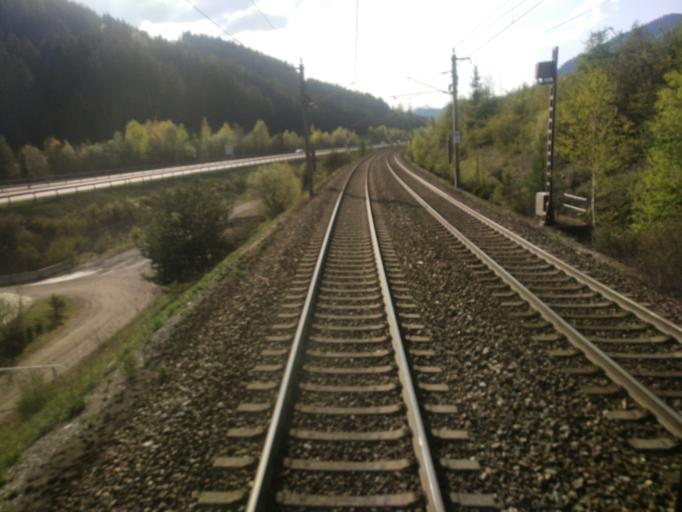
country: AT
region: Styria
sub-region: Politischer Bezirk Leoben
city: Kammern im Liesingtal
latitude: 47.3878
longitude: 14.8889
